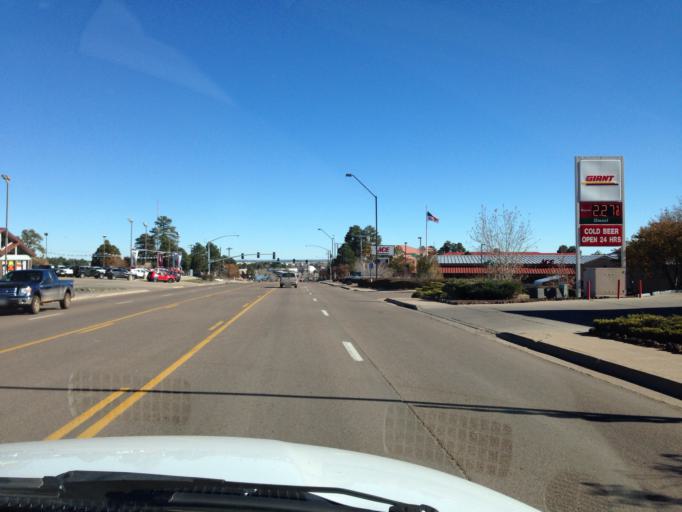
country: US
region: Arizona
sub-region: Navajo County
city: Show Low
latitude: 34.2483
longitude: -110.0464
